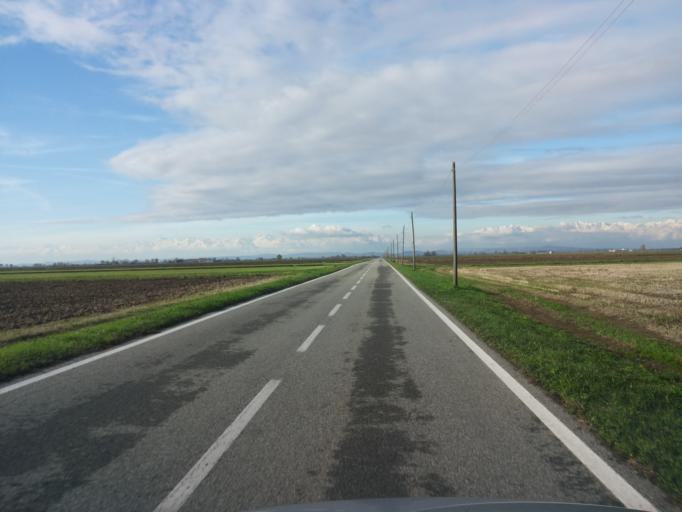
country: IT
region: Piedmont
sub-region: Provincia di Vercelli
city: Salasco
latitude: 45.2864
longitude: 8.2367
